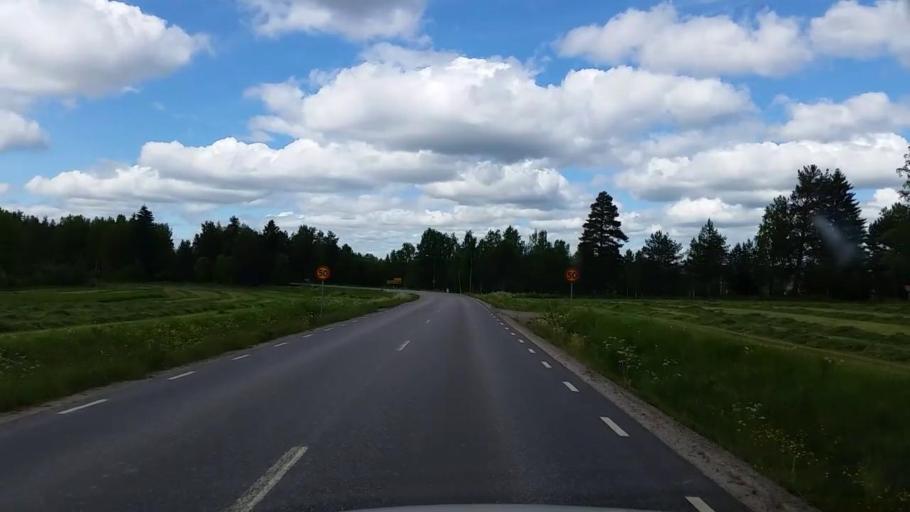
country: SE
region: Gaevleborg
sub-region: Ovanakers Kommun
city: Alfta
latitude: 61.3884
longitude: 16.0484
